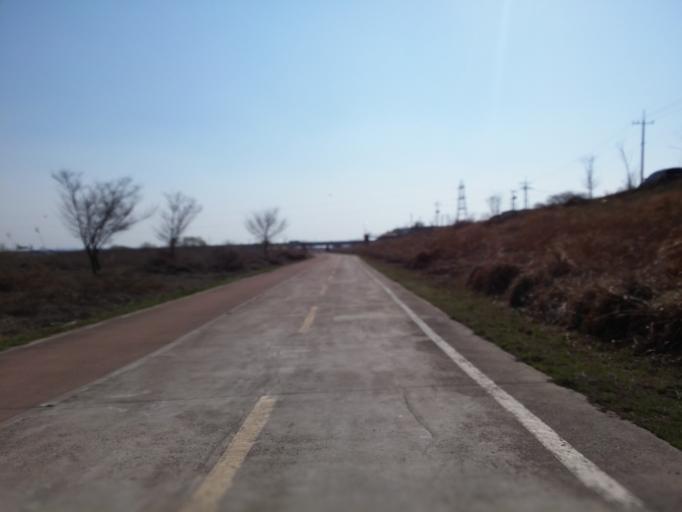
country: KR
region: Chungcheongbuk-do
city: Cheongju-si
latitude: 36.6553
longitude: 127.3776
